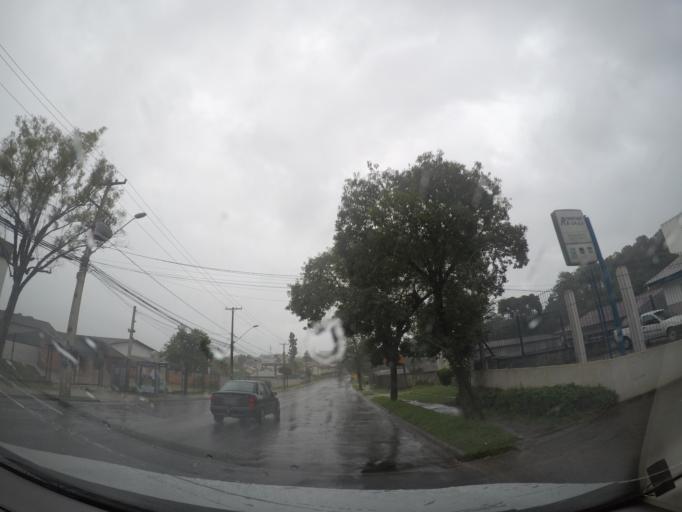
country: BR
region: Parana
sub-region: Curitiba
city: Curitiba
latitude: -25.4511
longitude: -49.3564
